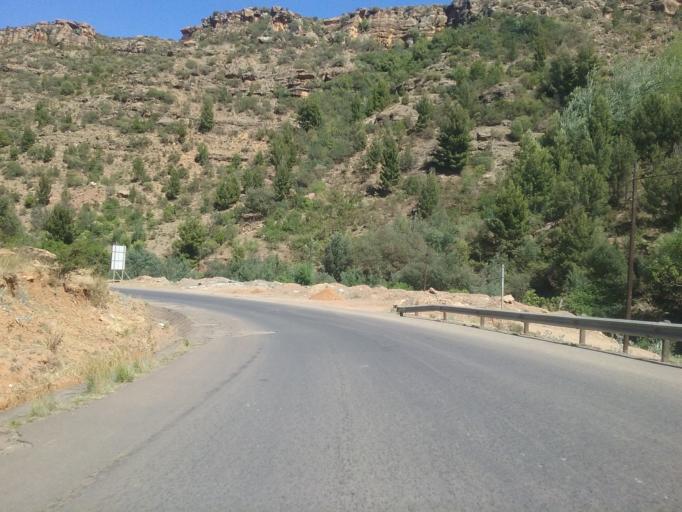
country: LS
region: Quthing
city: Quthing
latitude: -30.3986
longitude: 27.6873
